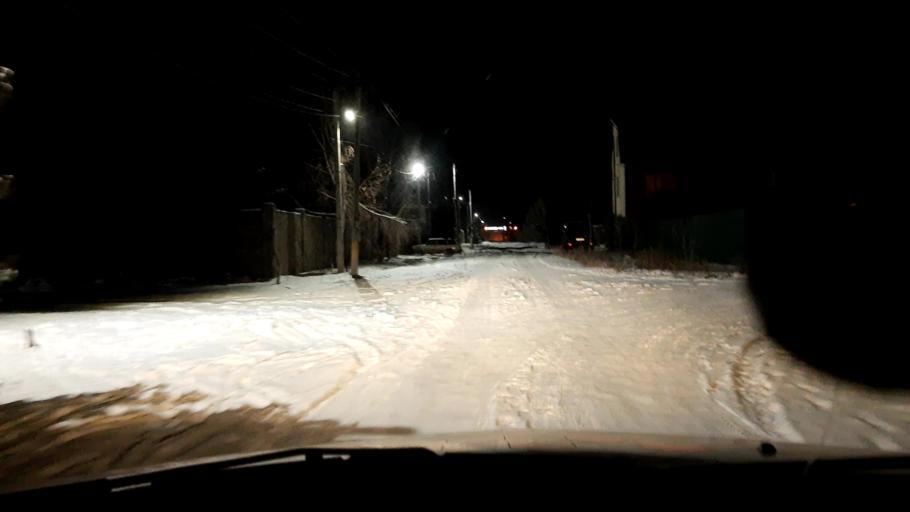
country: RU
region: Bashkortostan
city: Ufa
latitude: 54.6222
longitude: 55.9207
